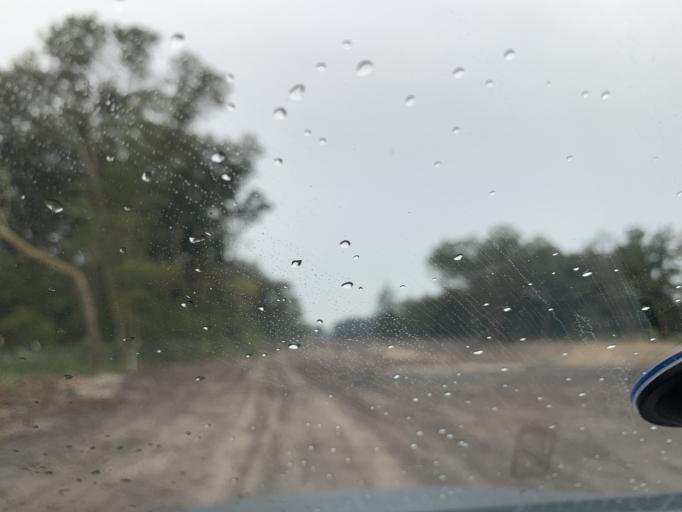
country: US
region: Florida
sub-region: Hernando County
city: Masaryktown
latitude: 28.4518
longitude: -82.4588
